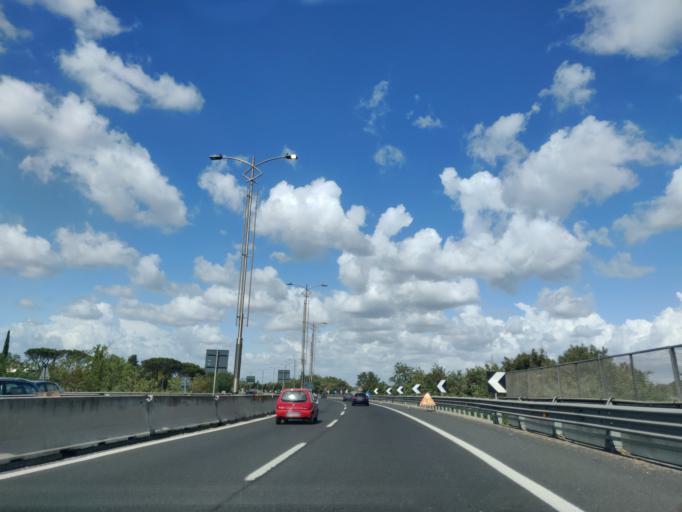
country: IT
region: Latium
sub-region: Citta metropolitana di Roma Capitale
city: Vitinia
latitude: 41.8209
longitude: 12.4156
